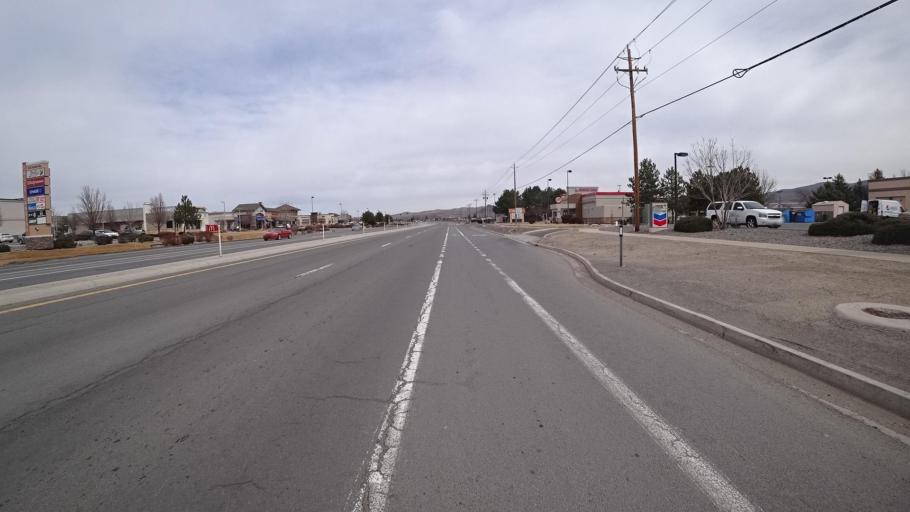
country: US
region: Nevada
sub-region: Washoe County
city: Spanish Springs
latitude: 39.6387
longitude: -119.7114
